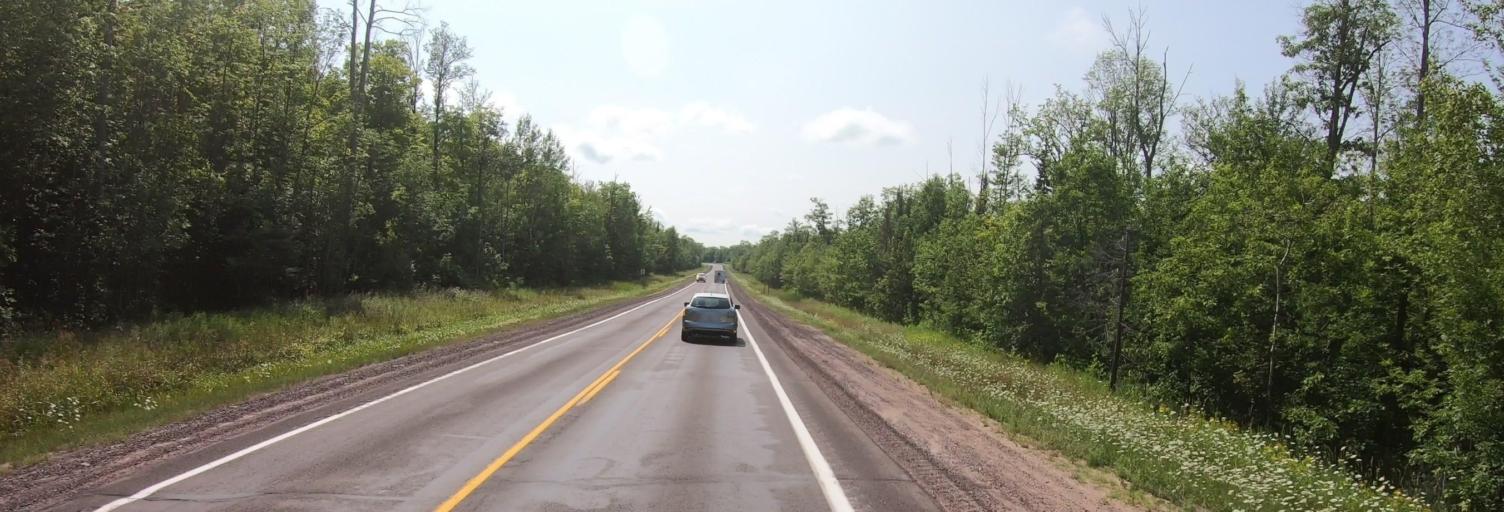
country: US
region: Michigan
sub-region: Ontonagon County
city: Ontonagon
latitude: 46.8611
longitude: -88.9435
